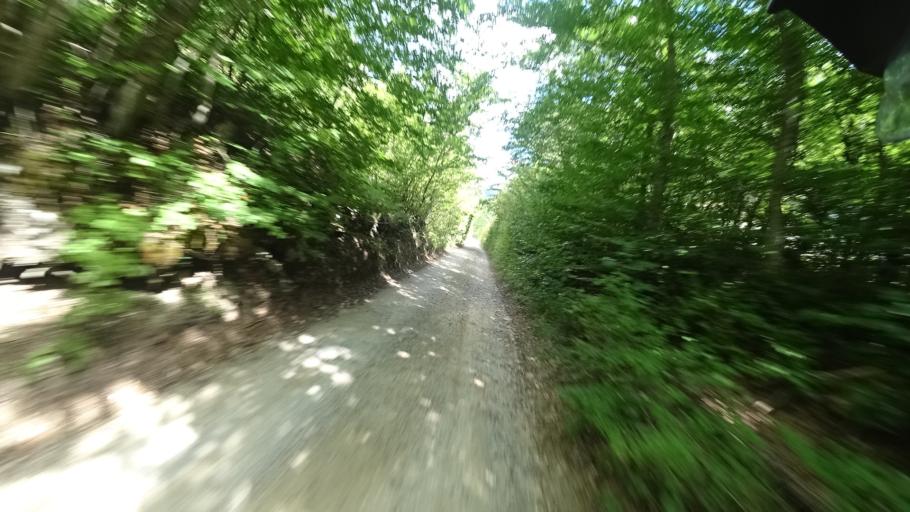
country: BA
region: Federation of Bosnia and Herzegovina
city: Orasac
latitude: 44.5629
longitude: 15.8331
